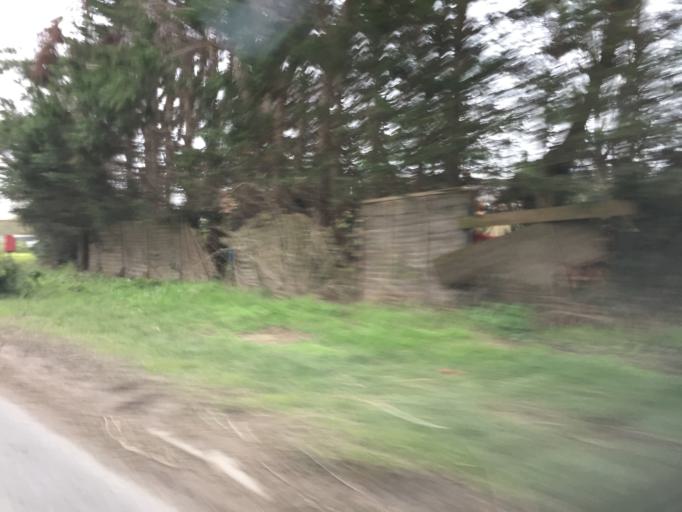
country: GB
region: England
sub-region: Oxfordshire
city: Stanford in the Vale
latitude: 51.6139
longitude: -1.4902
